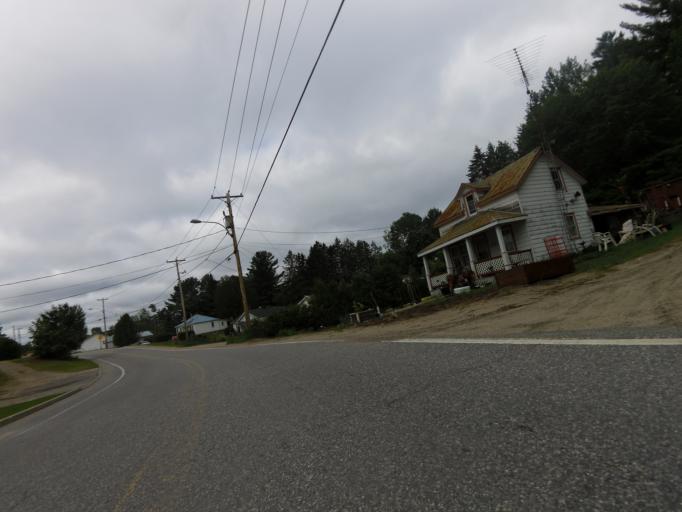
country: CA
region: Quebec
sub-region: Outaouais
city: Shawville
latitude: 45.8545
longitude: -76.4293
